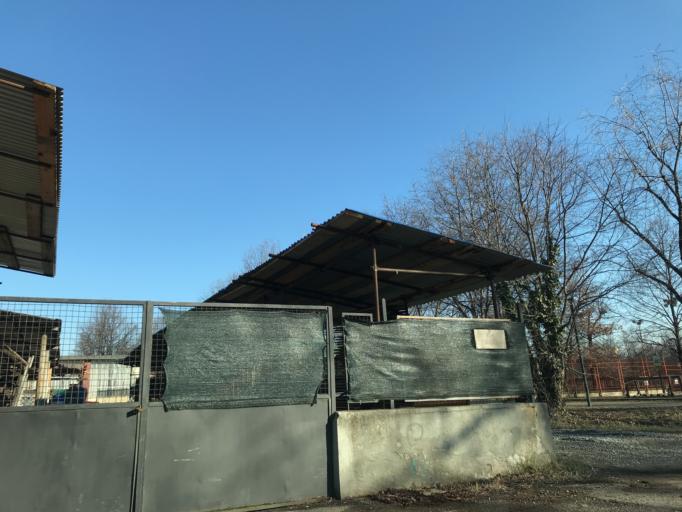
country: IT
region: Piedmont
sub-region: Provincia di Torino
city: Gerbido
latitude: 45.0477
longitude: 7.6187
